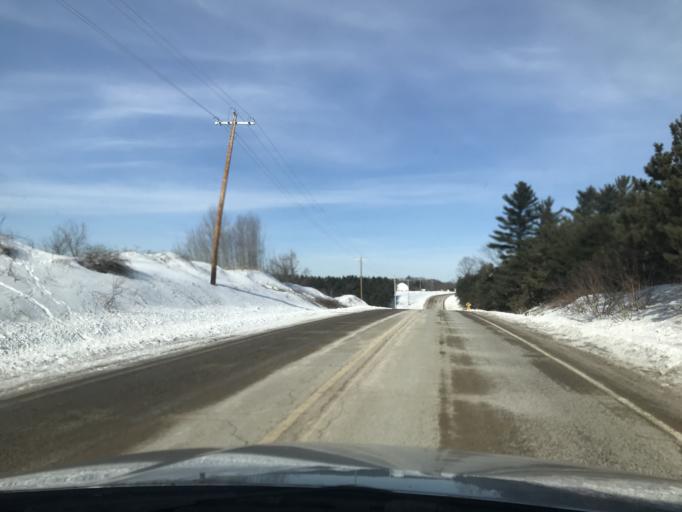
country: US
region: Wisconsin
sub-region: Oconto County
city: Oconto Falls
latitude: 45.1436
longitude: -88.1771
